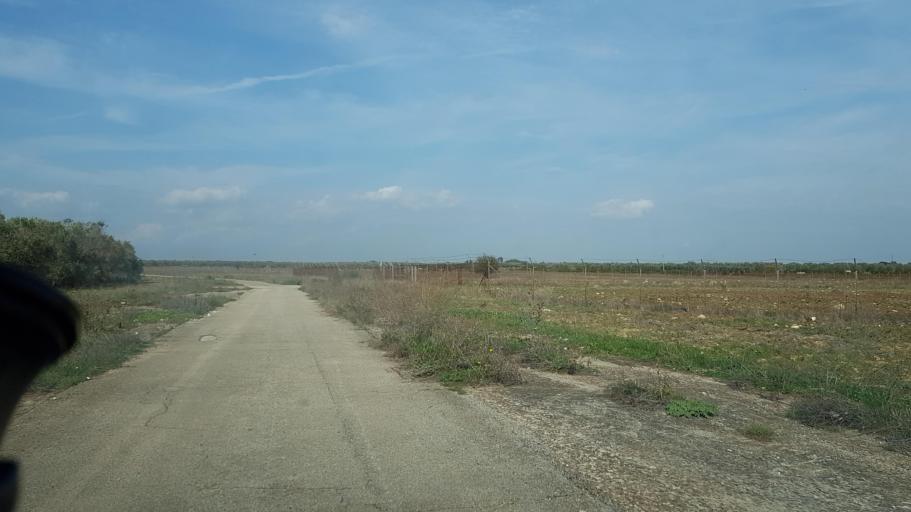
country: IT
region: Apulia
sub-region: Provincia di Brindisi
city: San Pancrazio Salentino
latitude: 40.4406
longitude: 17.8513
